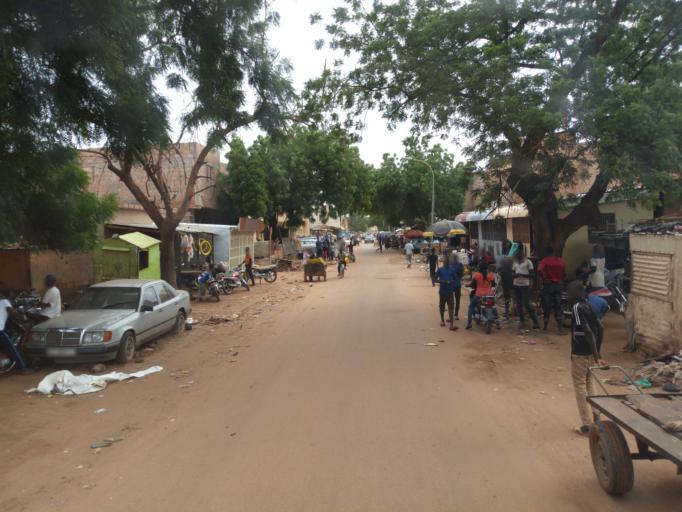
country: NE
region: Niamey
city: Niamey
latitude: 13.5193
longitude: 2.1148
